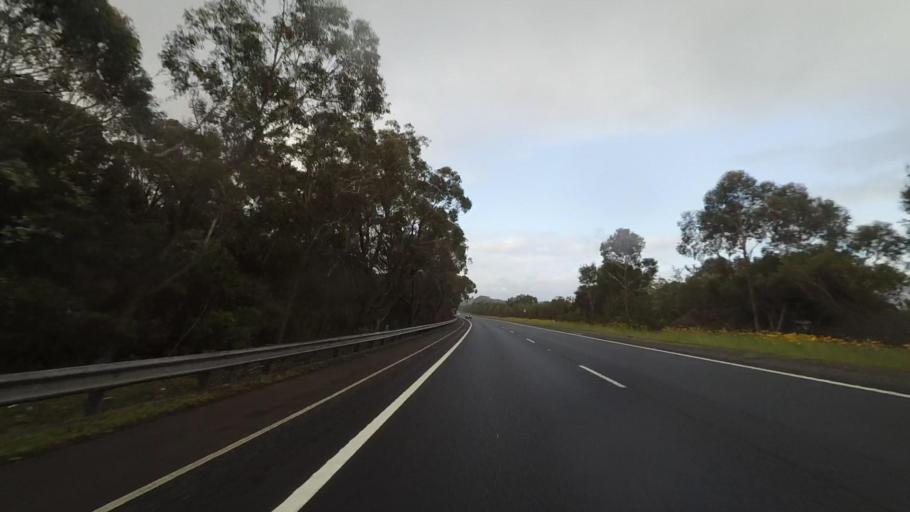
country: AU
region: New South Wales
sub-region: Wollongong
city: Helensburgh
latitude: -34.2360
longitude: 150.9464
